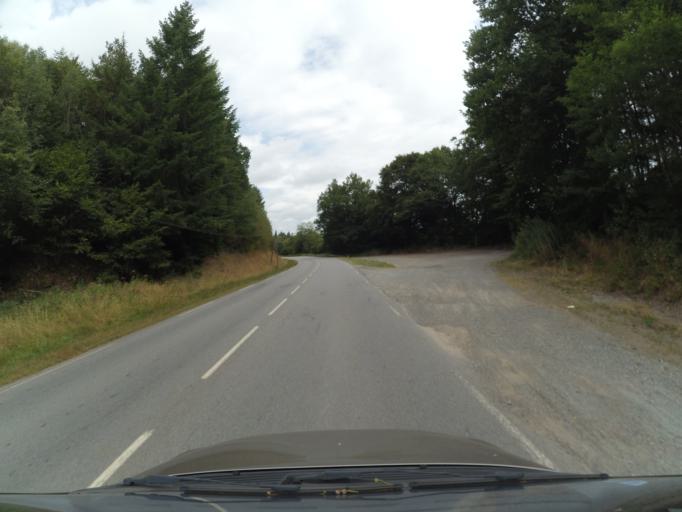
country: FR
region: Limousin
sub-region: Departement de la Correze
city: Ussel
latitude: 45.5804
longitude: 2.2924
